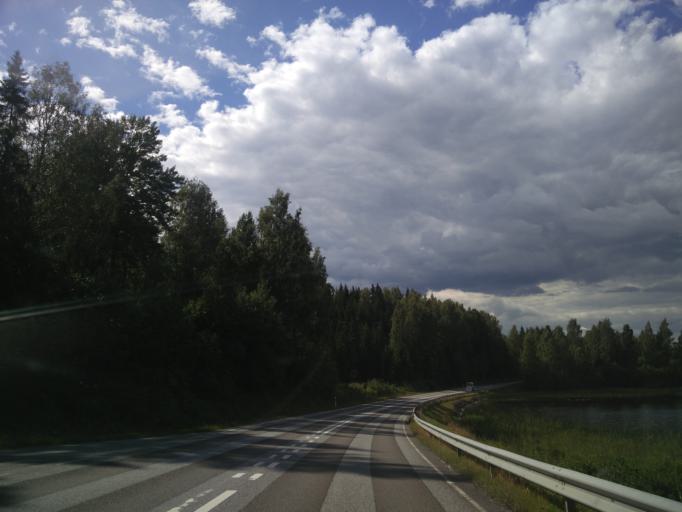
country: SE
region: OErebro
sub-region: Hallefors Kommun
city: Haellefors
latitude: 59.7441
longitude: 14.4543
